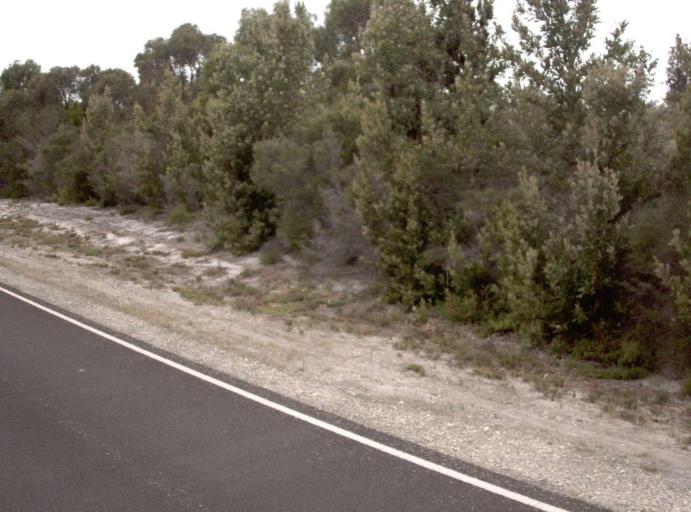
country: AU
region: Victoria
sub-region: Wellington
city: Sale
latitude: -38.1849
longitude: 147.3722
